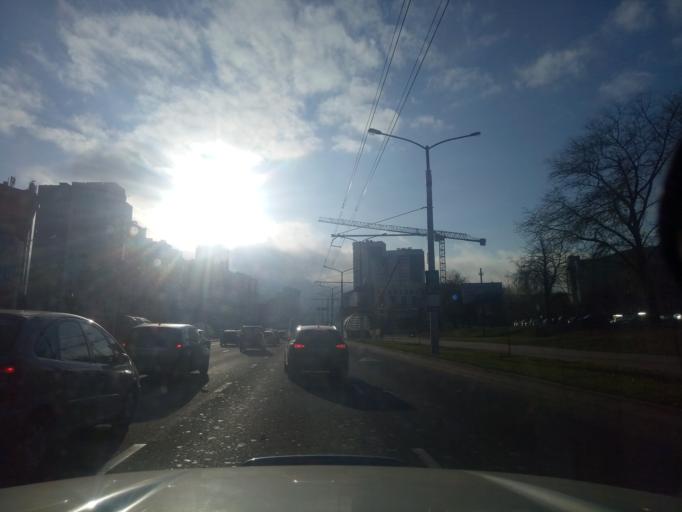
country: BY
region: Minsk
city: Minsk
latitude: 53.8919
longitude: 27.5261
